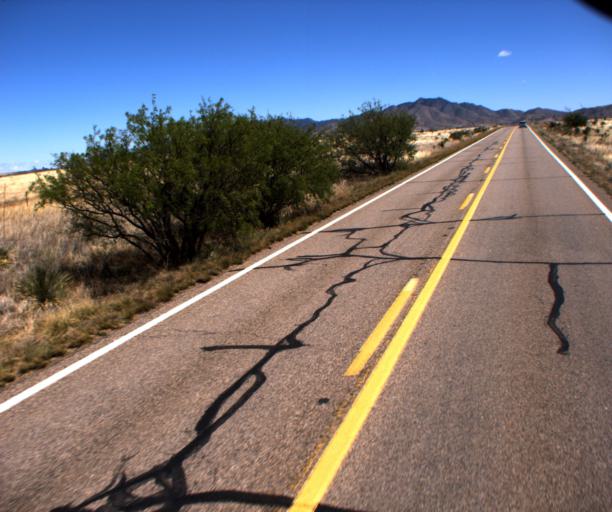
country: US
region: Arizona
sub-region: Cochise County
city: Huachuca City
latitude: 31.7195
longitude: -110.5413
